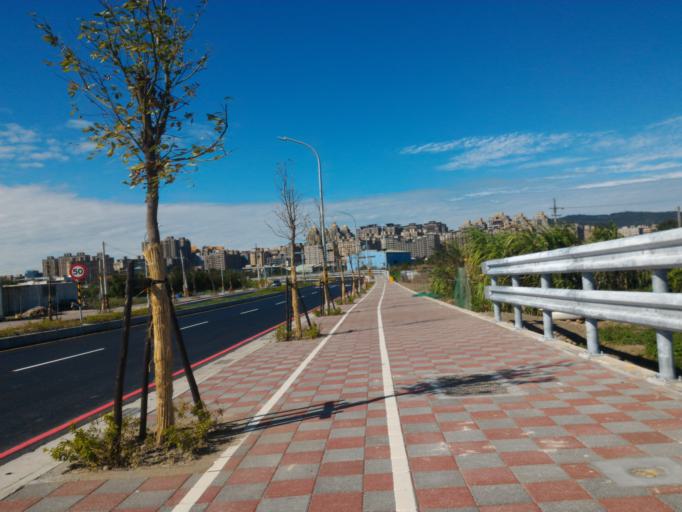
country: TW
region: Taiwan
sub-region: Taoyuan
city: Taoyuan
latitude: 24.9382
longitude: 121.3880
